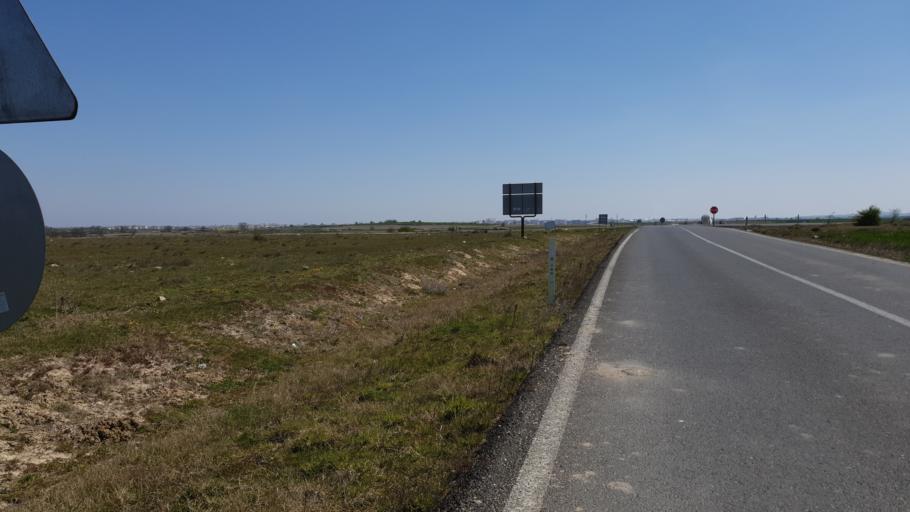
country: TR
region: Tekirdag
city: Velimese
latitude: 41.3270
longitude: 27.9229
